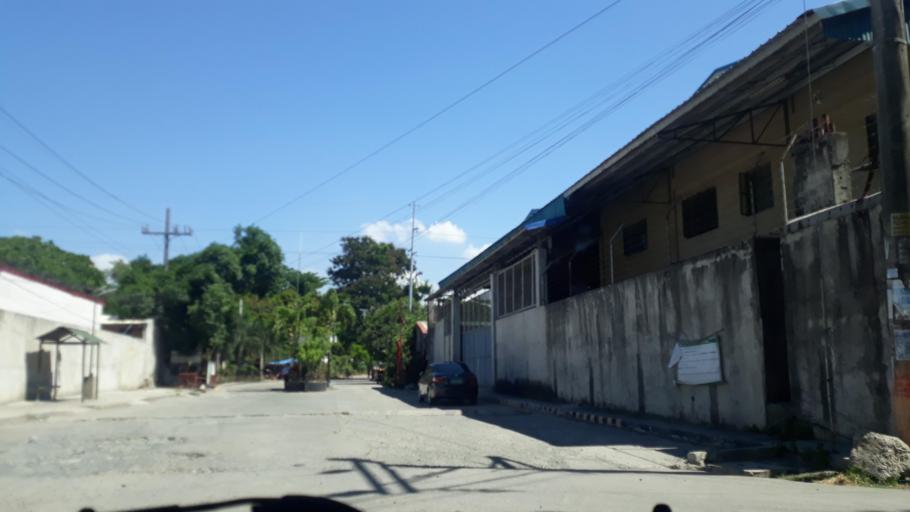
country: PH
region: Calabarzon
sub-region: Province of Cavite
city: Manggahan
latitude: 14.2983
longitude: 120.9173
